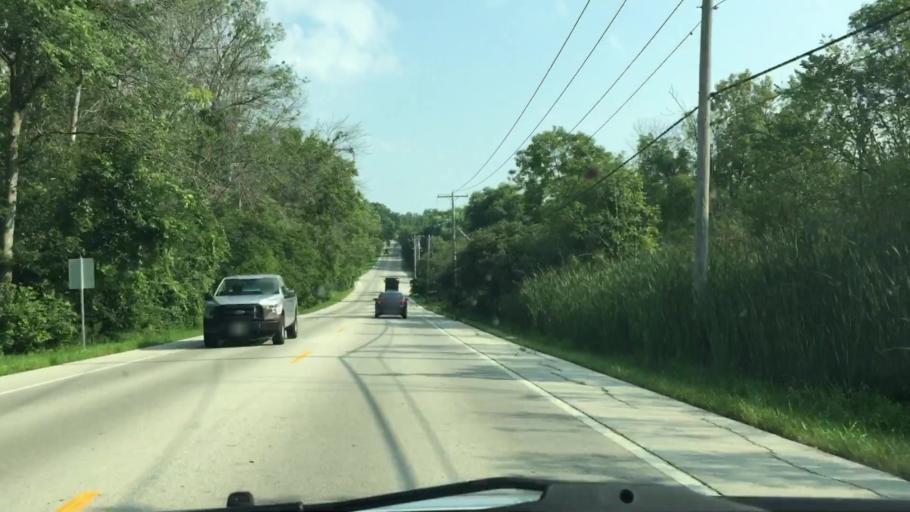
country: US
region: Wisconsin
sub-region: Waukesha County
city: Brookfield
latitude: 43.0453
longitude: -88.1465
